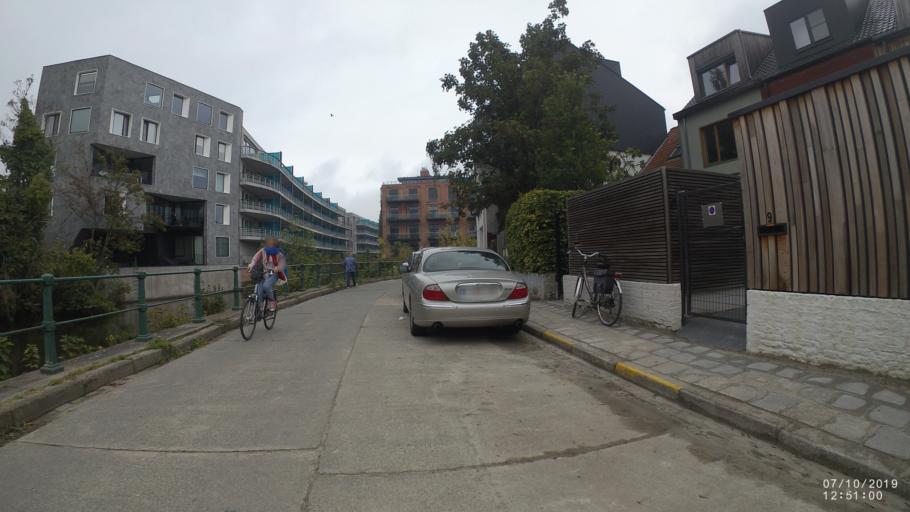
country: BE
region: Flanders
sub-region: Provincie Oost-Vlaanderen
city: Ledeberg
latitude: 51.0391
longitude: 3.7393
